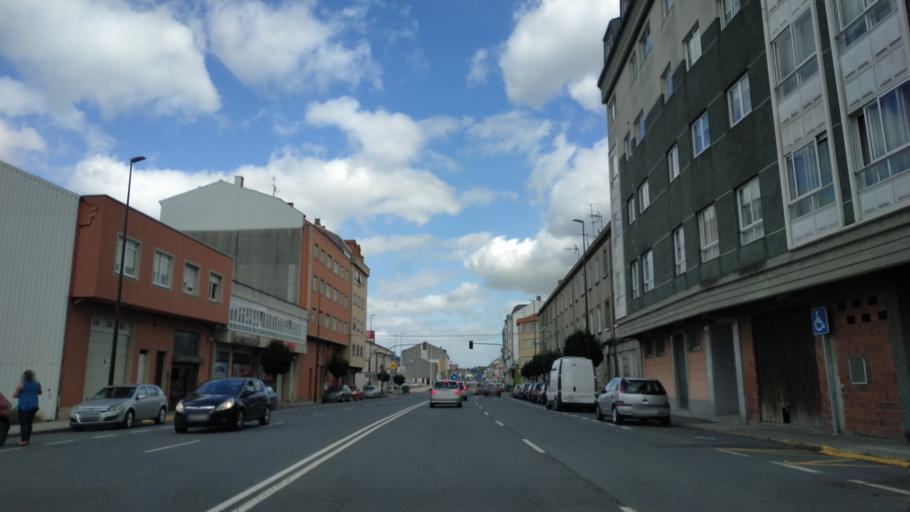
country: ES
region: Galicia
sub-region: Provincia da Coruna
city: Carballo
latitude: 43.2205
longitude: -8.6862
